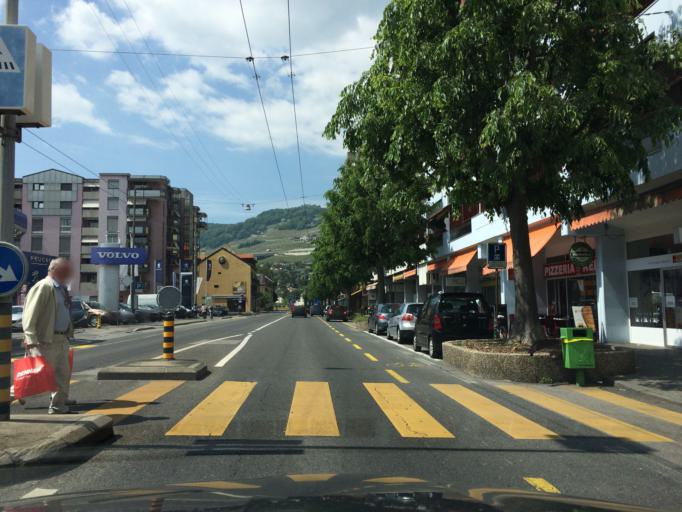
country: CH
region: Vaud
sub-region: Riviera-Pays-d'Enhaut District
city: Vevey
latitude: 46.4652
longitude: 6.8387
